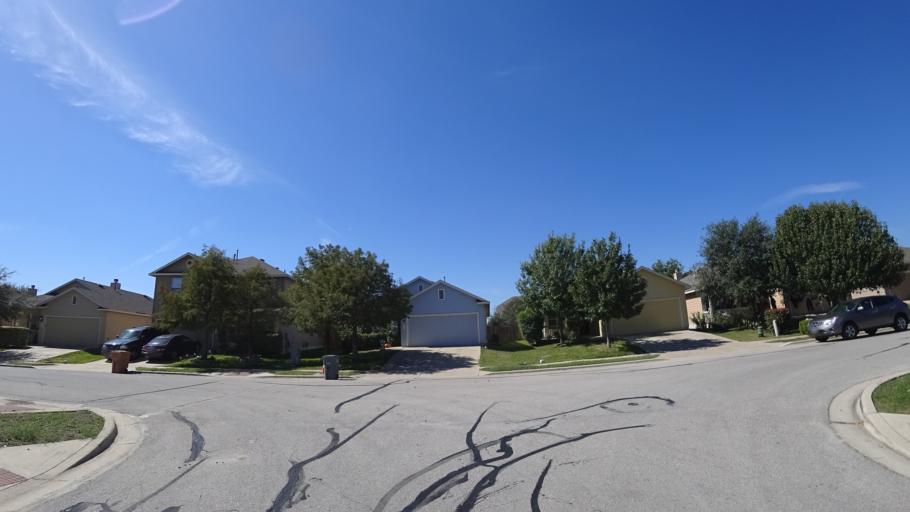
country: US
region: Texas
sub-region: Travis County
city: Austin
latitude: 30.1981
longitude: -97.6969
